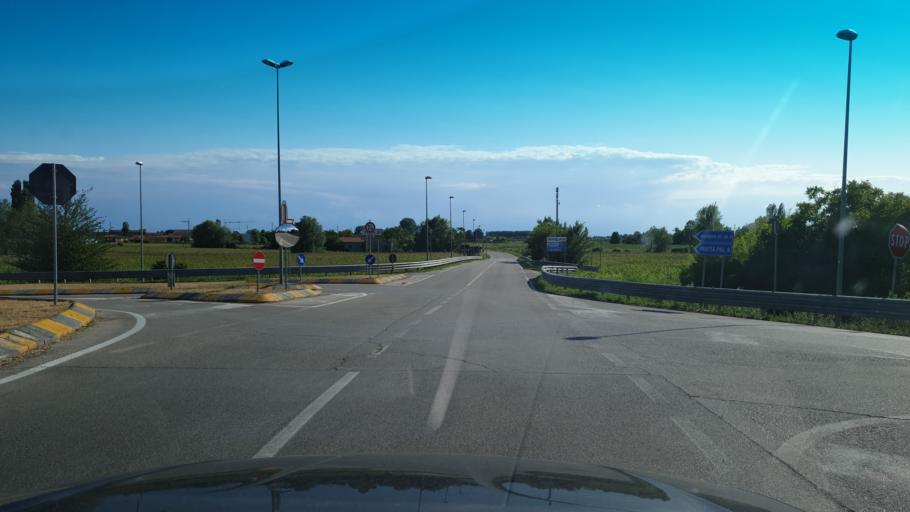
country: IT
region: Veneto
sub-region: Provincia di Rovigo
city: Costa di Rovigo
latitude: 45.0555
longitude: 11.6945
